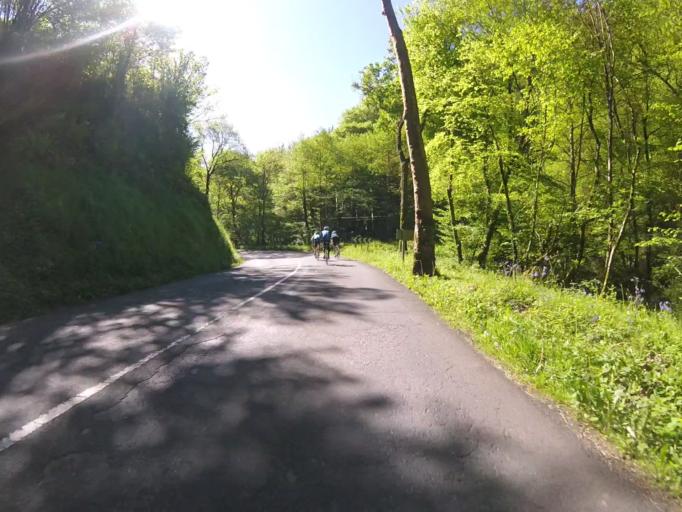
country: ES
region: Basque Country
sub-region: Provincia de Guipuzcoa
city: Errezil
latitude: 43.1740
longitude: -2.2022
